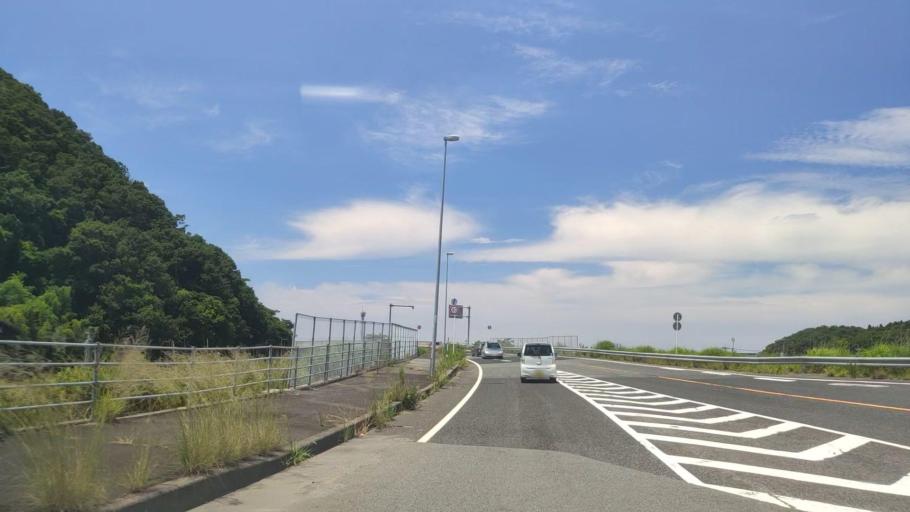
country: JP
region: Tottori
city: Tottori
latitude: 35.4706
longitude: 134.2423
